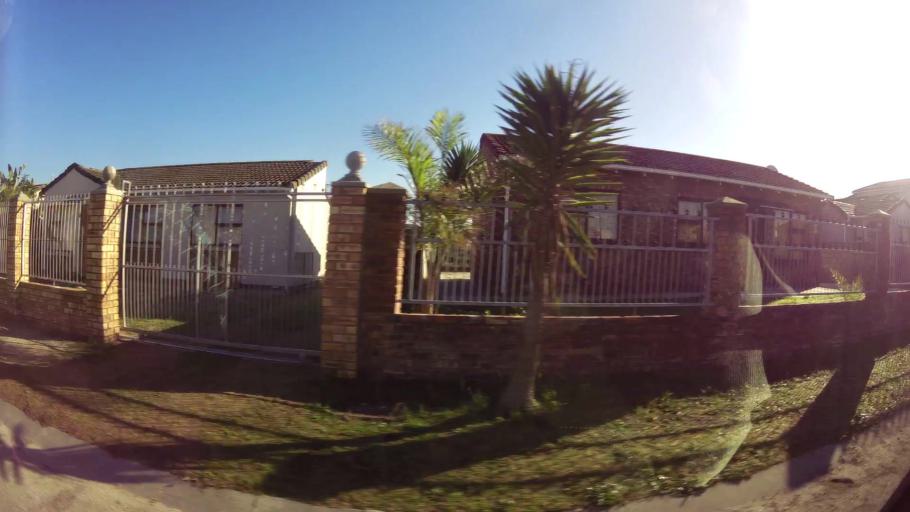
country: ZA
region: Eastern Cape
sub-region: Nelson Mandela Bay Metropolitan Municipality
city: Port Elizabeth
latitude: -33.9778
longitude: 25.6294
